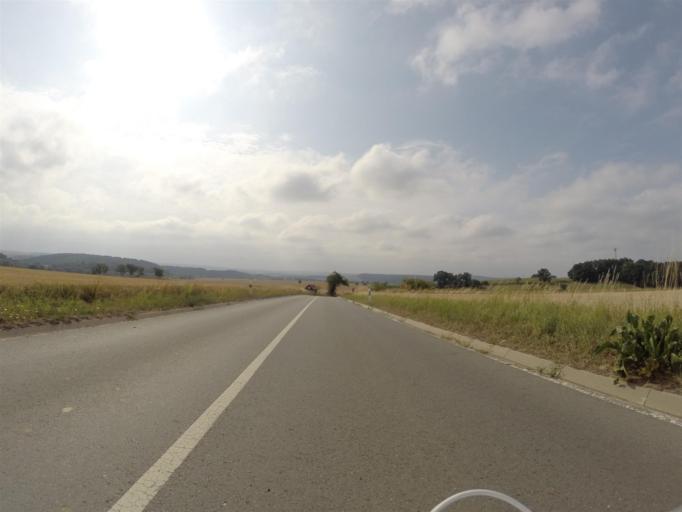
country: DE
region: Thuringia
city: Schloben
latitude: 50.8872
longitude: 11.6909
